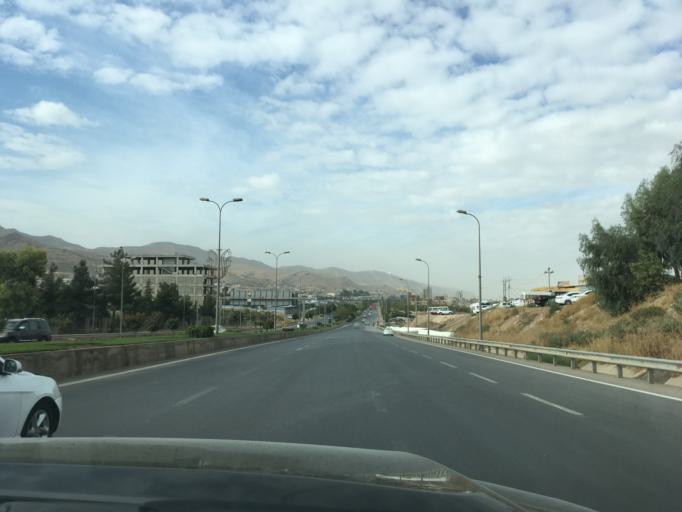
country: IQ
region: Dahuk
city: Sinah
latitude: 36.8495
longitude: 43.0463
